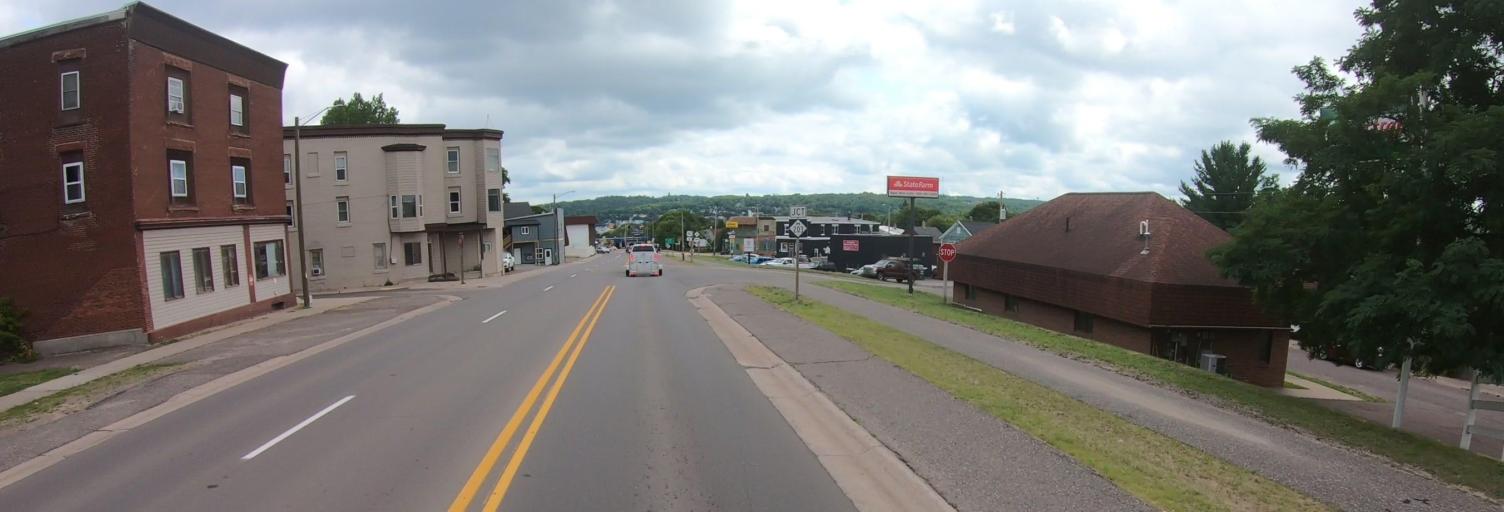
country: US
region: Michigan
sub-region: Houghton County
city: Hancock
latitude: 47.1276
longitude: -88.5955
